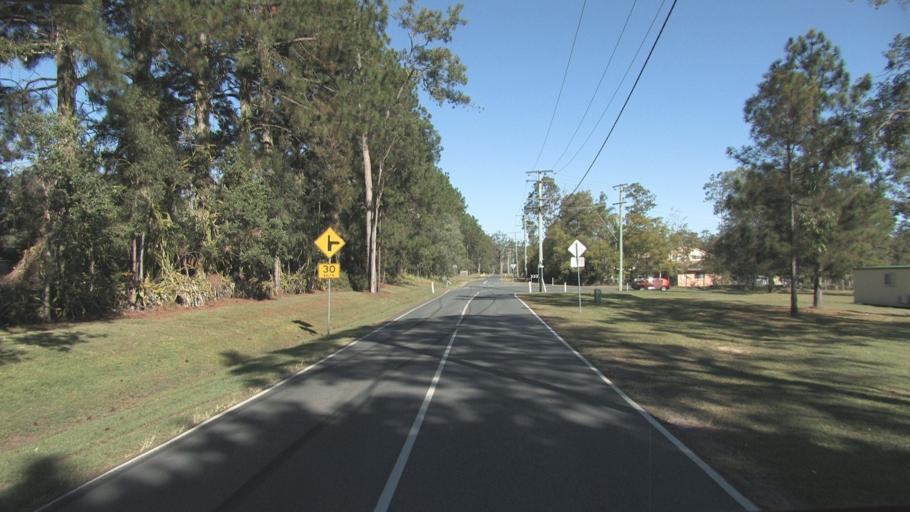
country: AU
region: Queensland
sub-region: Logan
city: Logan Reserve
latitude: -27.7192
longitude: 153.0646
